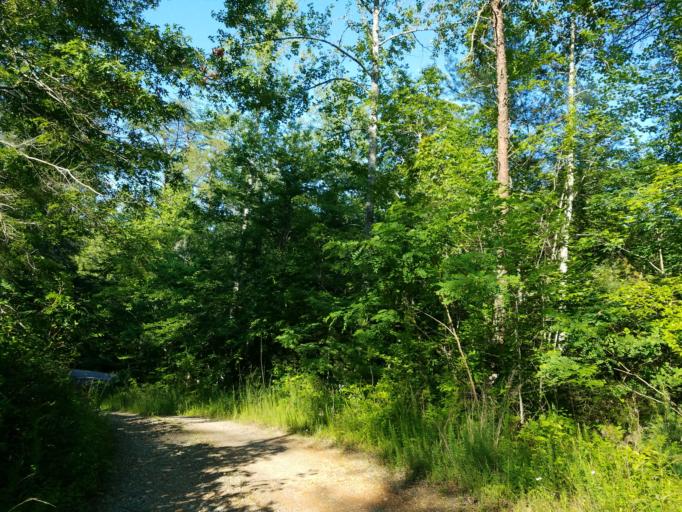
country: US
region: Georgia
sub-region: Fannin County
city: Blue Ridge
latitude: 34.7993
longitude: -84.1855
